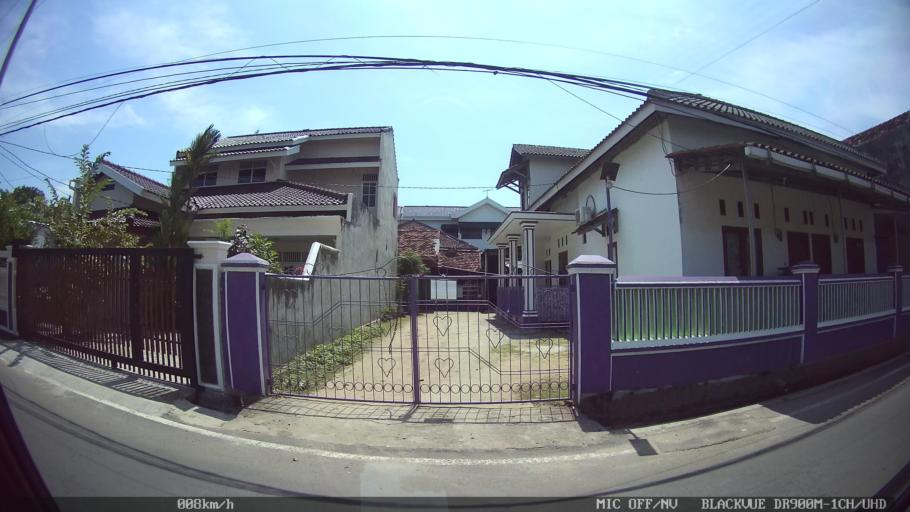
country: ID
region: Lampung
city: Kedaton
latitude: -5.3844
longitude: 105.2765
